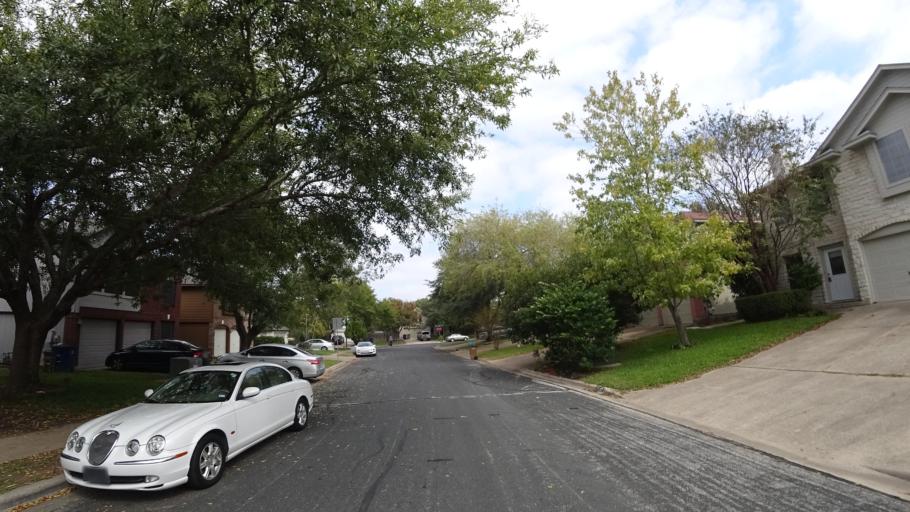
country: US
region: Texas
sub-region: Travis County
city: Shady Hollow
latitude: 30.1936
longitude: -97.8336
